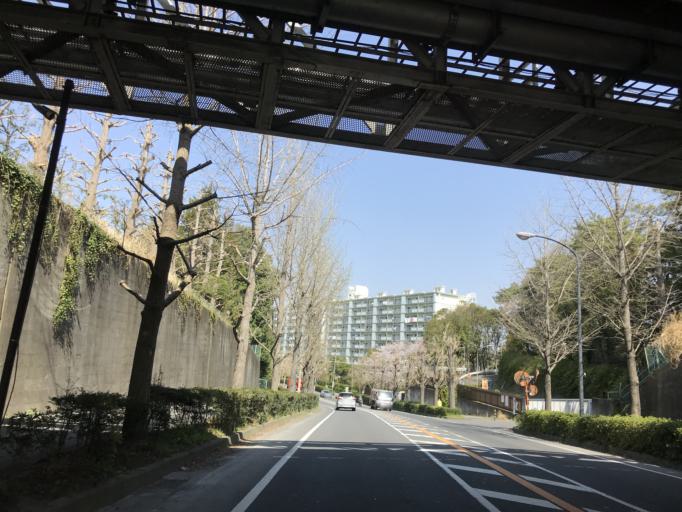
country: JP
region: Ibaraki
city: Toride
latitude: 35.9015
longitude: 140.0512
